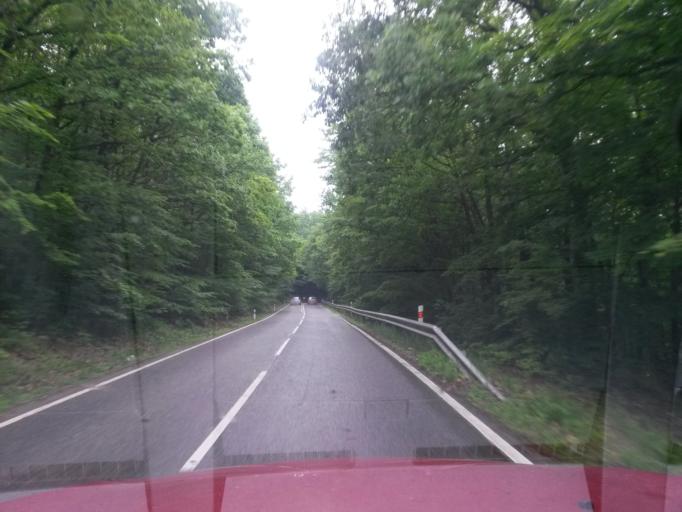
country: SK
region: Kosicky
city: Kosice
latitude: 48.7111
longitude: 21.1955
